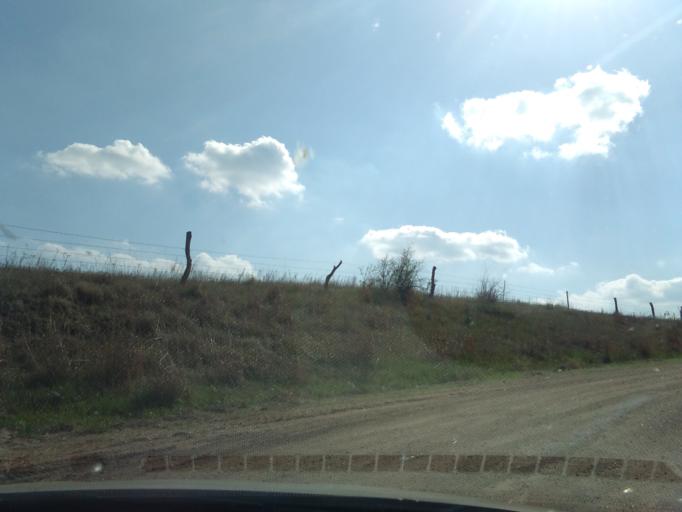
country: US
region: Nebraska
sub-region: Webster County
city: Red Cloud
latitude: 40.0025
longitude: -98.3296
